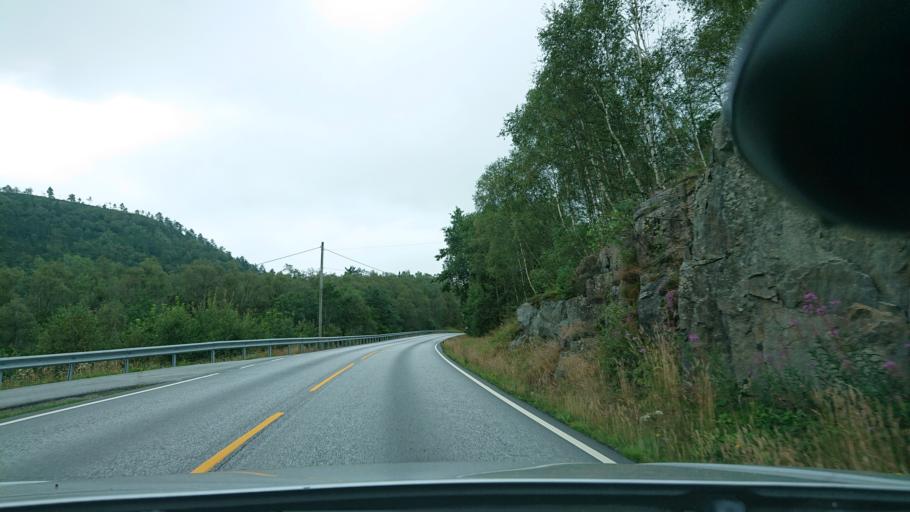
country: NO
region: Rogaland
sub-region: Hjelmeland
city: Hjelmelandsvagen
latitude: 59.1679
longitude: 6.1575
